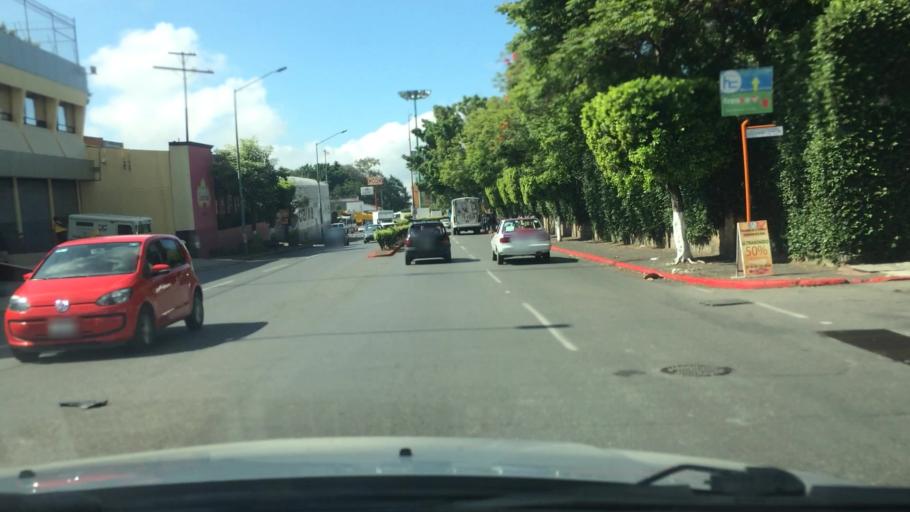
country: MX
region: Morelos
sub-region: Cuernavaca
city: Fraccionamiento Lomas de Ahuatlan
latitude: 18.9514
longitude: -99.2449
